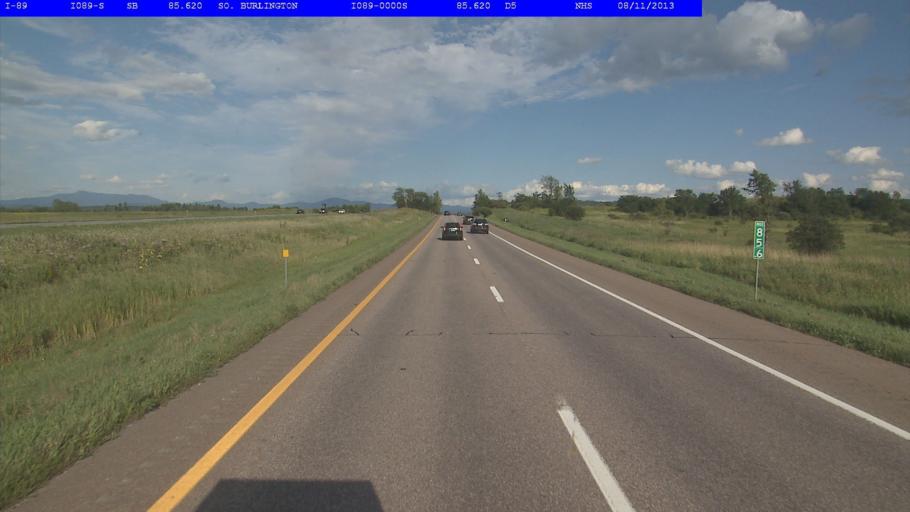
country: US
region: Vermont
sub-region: Chittenden County
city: South Burlington
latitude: 44.4453
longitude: -73.1471
